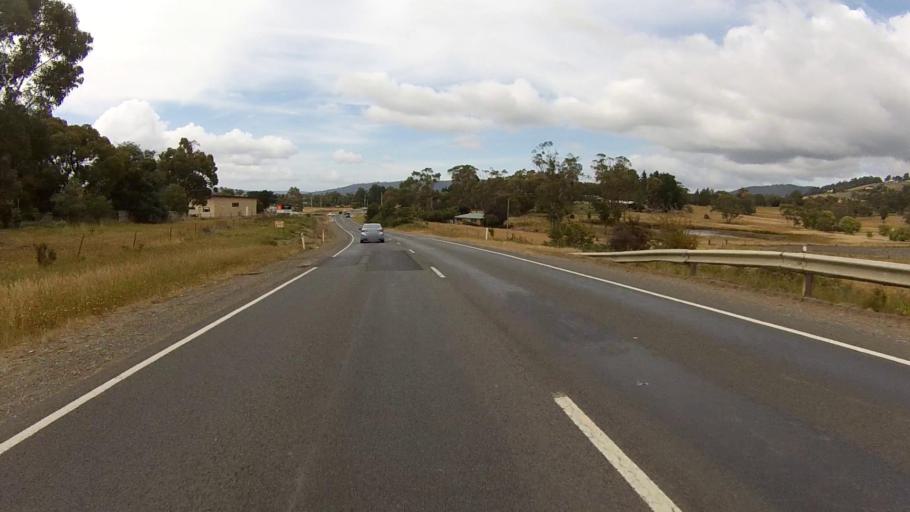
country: AU
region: Tasmania
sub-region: Kingborough
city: Margate
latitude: -43.0317
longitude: 147.2650
